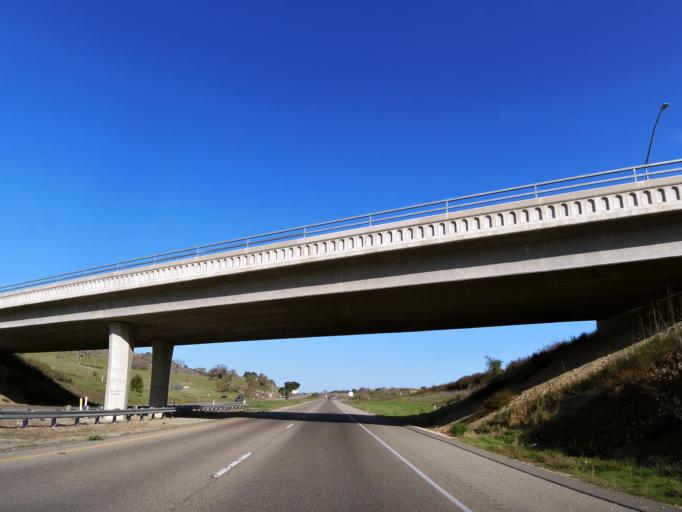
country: US
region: California
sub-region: Santa Barbara County
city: Los Olivos
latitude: 34.6875
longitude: -120.1574
